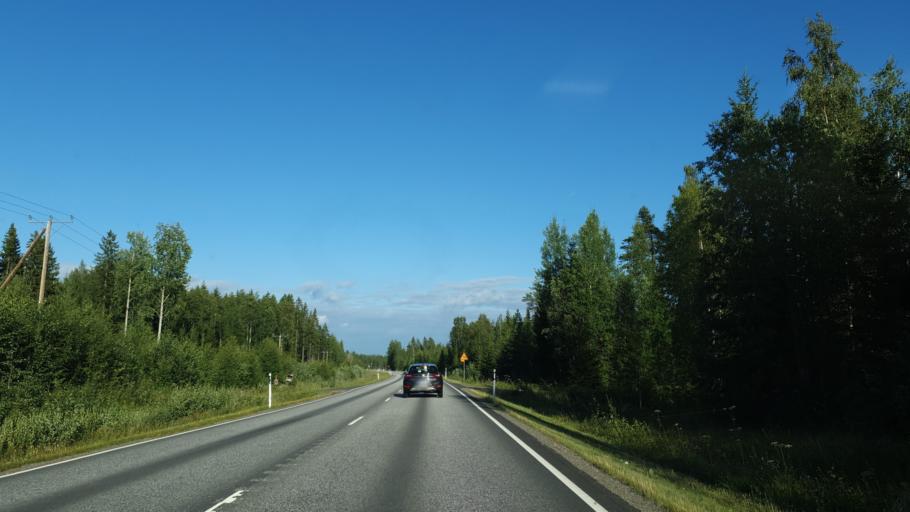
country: FI
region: North Karelia
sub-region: Joensuu
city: Outokumpu
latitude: 62.5332
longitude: 28.9598
